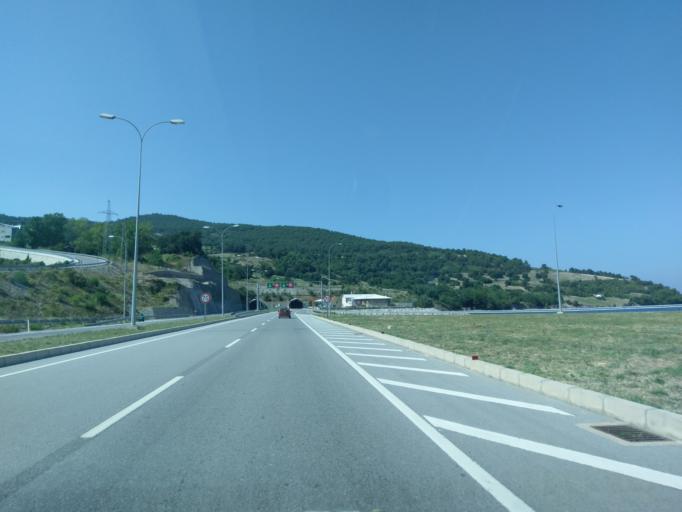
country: TR
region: Sinop
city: Dikmen
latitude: 41.7278
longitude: 35.2636
